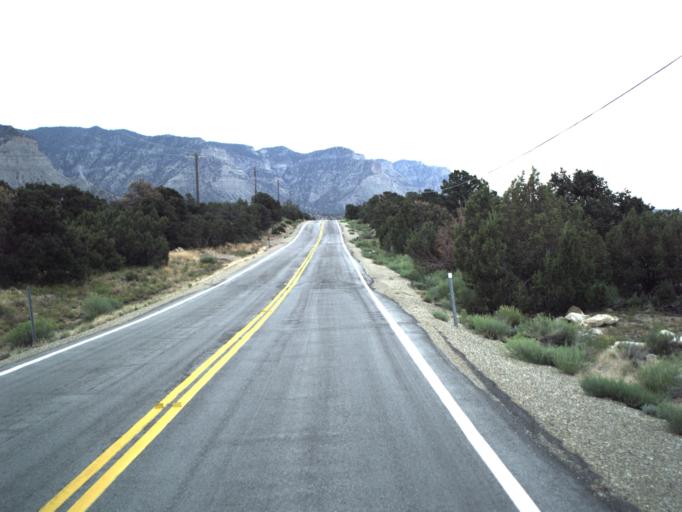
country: US
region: Utah
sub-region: Carbon County
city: East Carbon City
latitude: 39.5316
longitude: -110.4019
